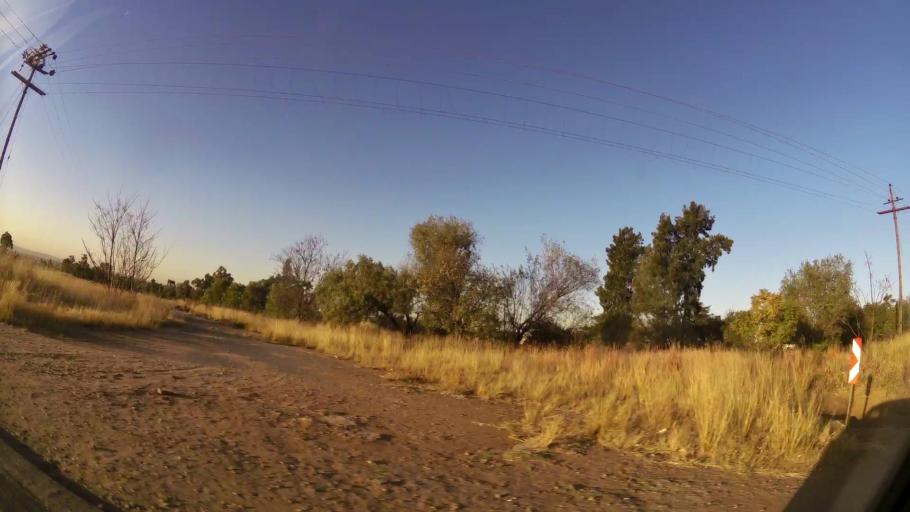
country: ZA
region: Gauteng
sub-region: City of Johannesburg Metropolitan Municipality
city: Diepsloot
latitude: -25.9285
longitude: 28.0436
